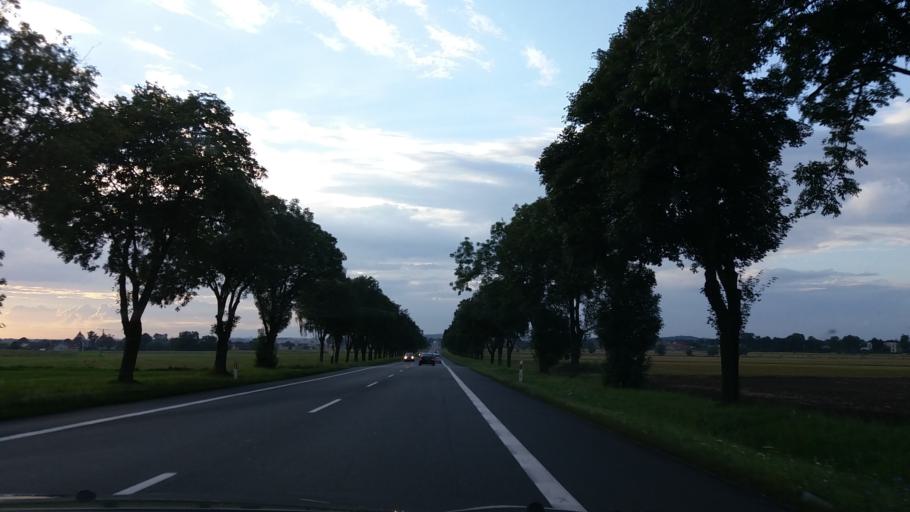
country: PL
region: Lower Silesian Voivodeship
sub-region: Powiat polkowicki
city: Radwanice
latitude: 51.6100
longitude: 15.9421
